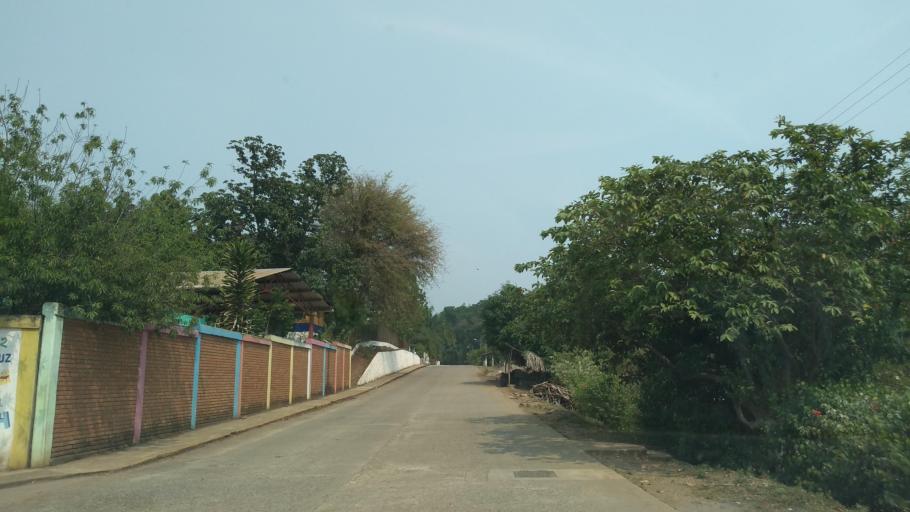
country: MX
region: Veracruz
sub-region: Tezonapa
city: Laguna Chica (Pueblo Nuevo)
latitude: 18.5432
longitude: -96.7765
